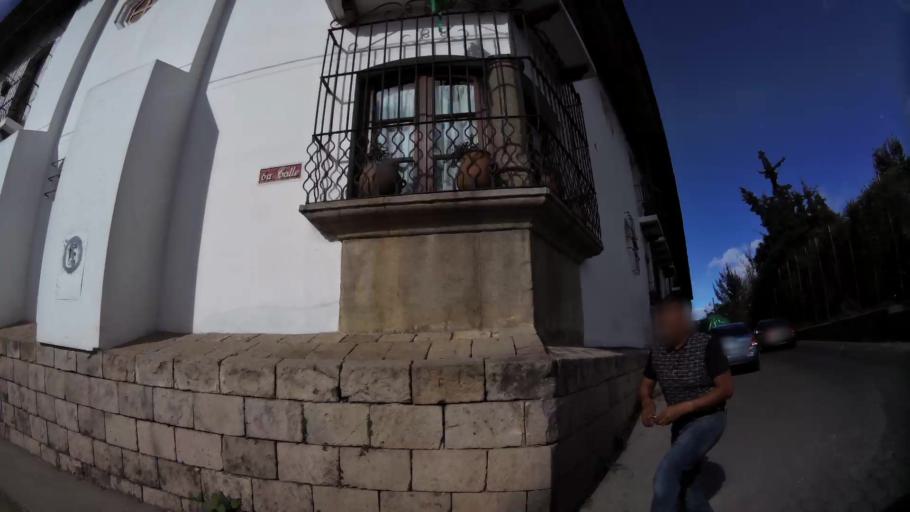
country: GT
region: Quiche
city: Chichicastenango
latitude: 14.9426
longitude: -91.1095
